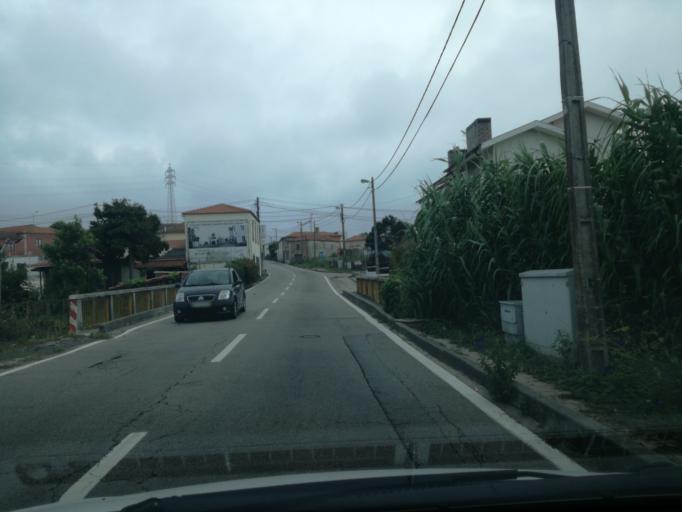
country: PT
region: Aveiro
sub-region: Espinho
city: Silvalde
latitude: 40.9980
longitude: -8.6359
